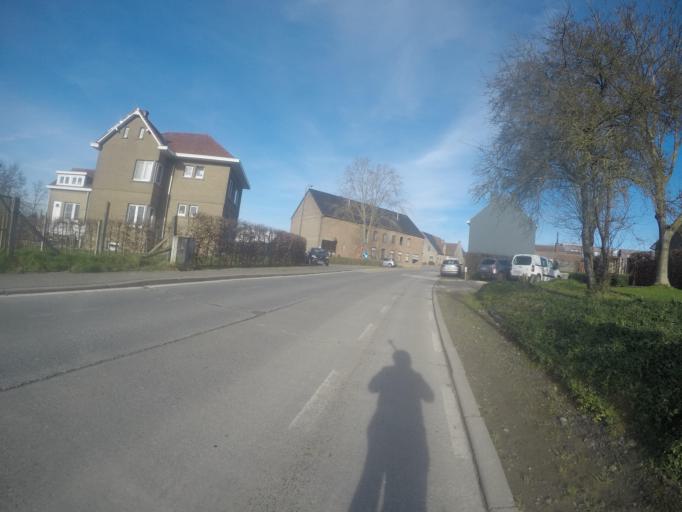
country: BE
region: Flanders
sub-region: Provincie Vlaams-Brabant
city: Pepingen
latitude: 50.7571
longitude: 4.1527
